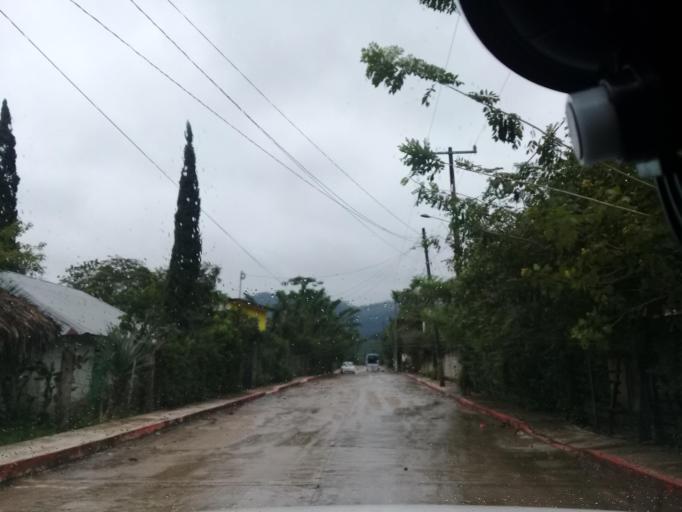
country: MX
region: Veracruz
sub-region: Chalma
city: San Pedro Coyutla
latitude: 21.2263
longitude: -98.4269
